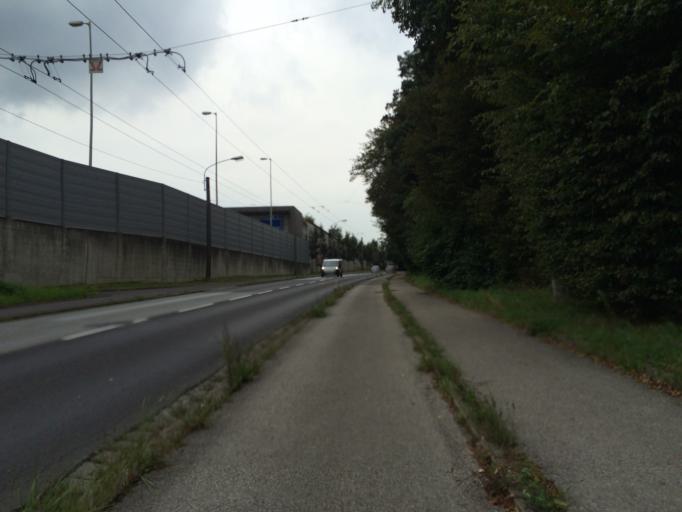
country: AT
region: Upper Austria
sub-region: Linz Stadt
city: Linz
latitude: 48.2770
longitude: 14.2942
